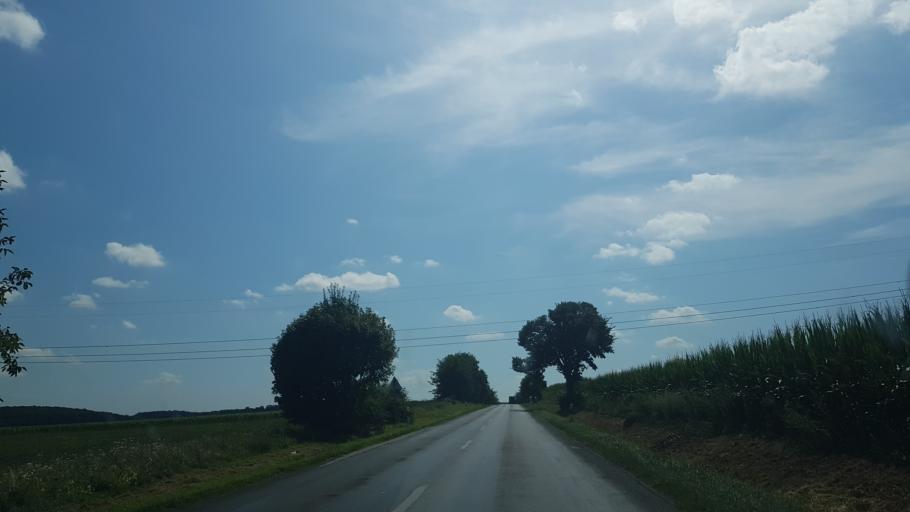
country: HU
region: Somogy
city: Bohonye
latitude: 46.4797
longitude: 17.4050
